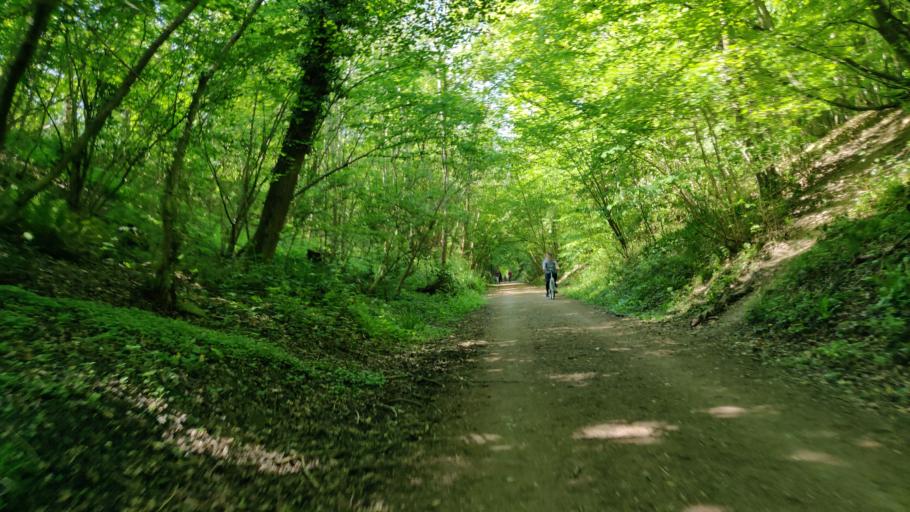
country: GB
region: England
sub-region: West Sussex
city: Rudgwick
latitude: 51.0724
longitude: -0.4239
